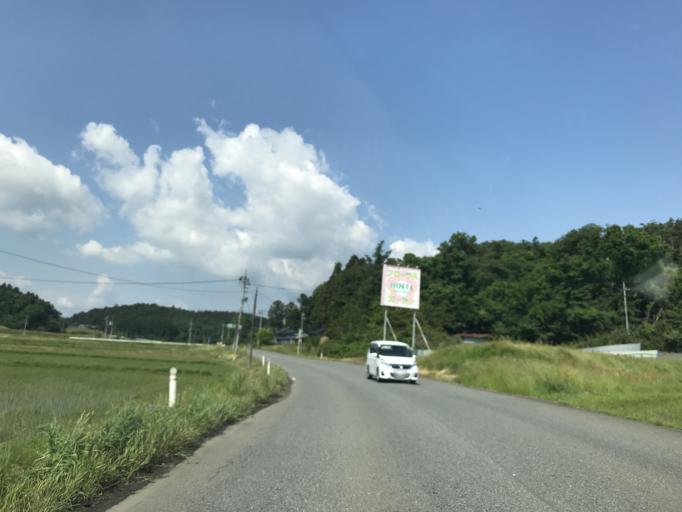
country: JP
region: Iwate
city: Ichinoseki
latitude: 38.7963
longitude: 141.0447
